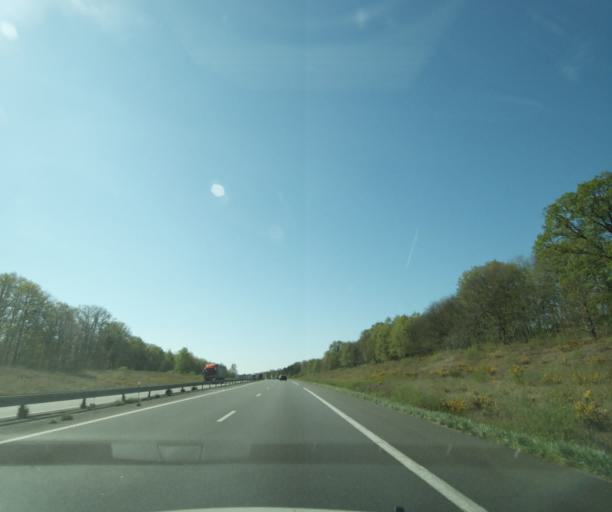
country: FR
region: Centre
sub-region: Departement du Loir-et-Cher
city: Nouan-le-Fuzelier
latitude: 47.5021
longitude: 2.0069
